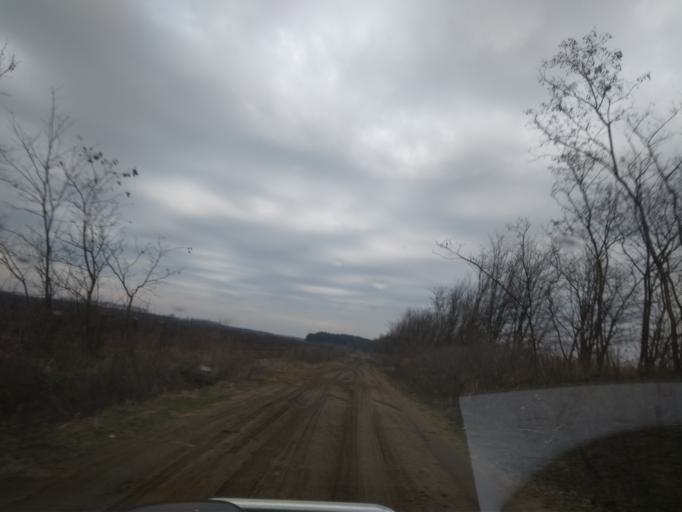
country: HU
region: Szabolcs-Szatmar-Bereg
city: Nyirpazony
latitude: 47.9892
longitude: 21.7887
